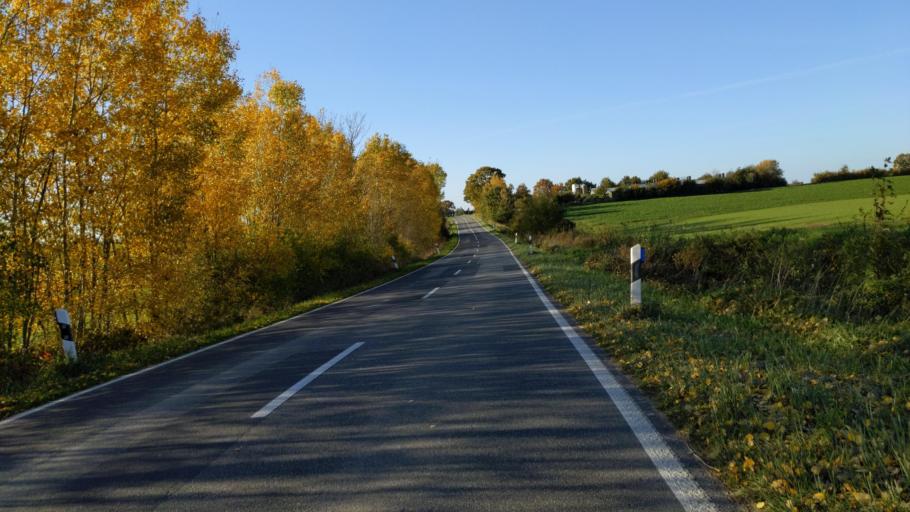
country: DE
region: Schleswig-Holstein
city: Gross Sarau
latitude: 53.7728
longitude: 10.7209
